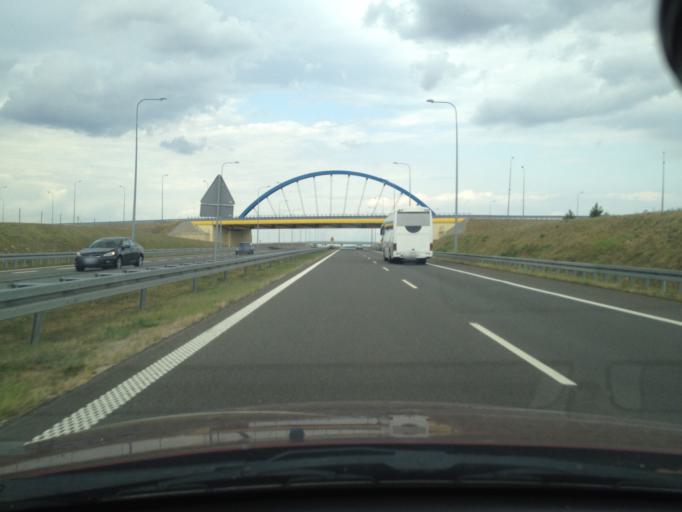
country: PL
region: West Pomeranian Voivodeship
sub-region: Powiat pyrzycki
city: Bielice
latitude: 53.1215
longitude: 14.7411
